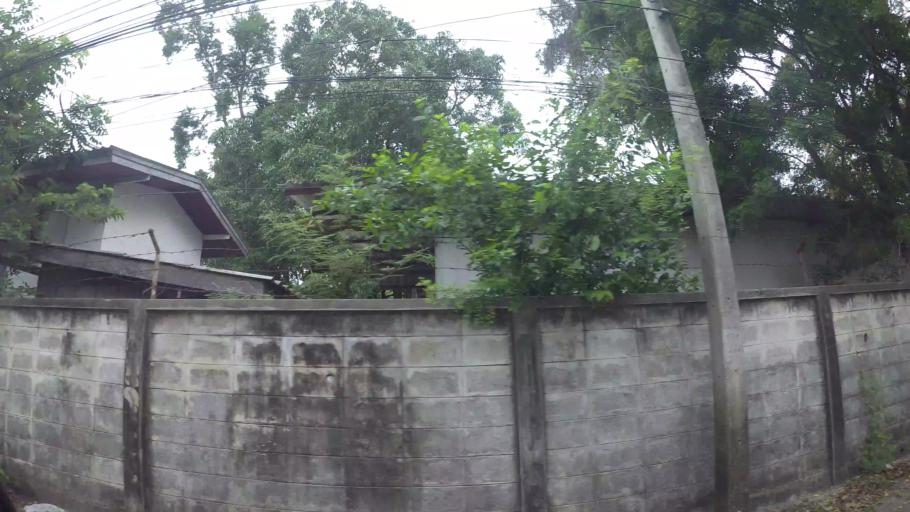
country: TH
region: Rayong
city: Rayong
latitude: 12.6678
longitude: 101.2757
